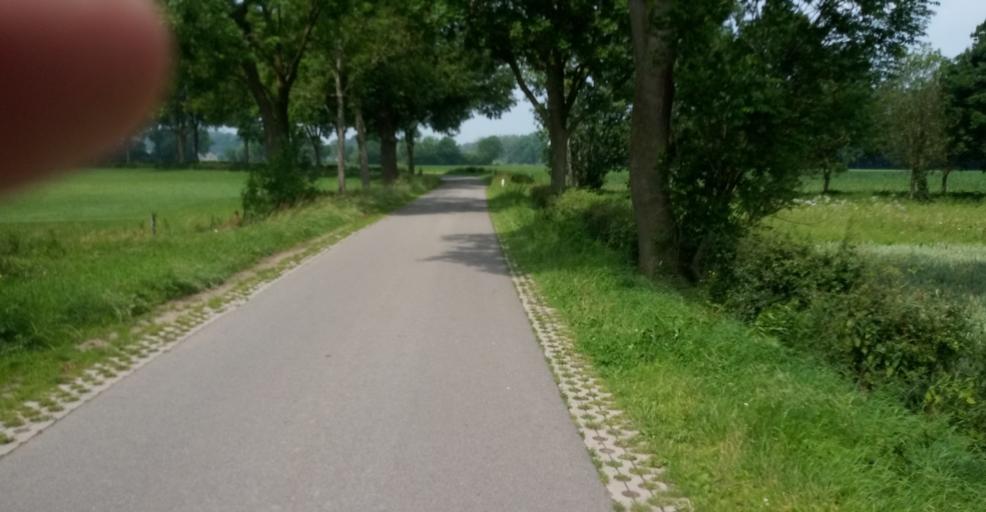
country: NL
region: Gelderland
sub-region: Gemeente Voorst
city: Voorst
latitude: 52.1759
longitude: 6.1560
